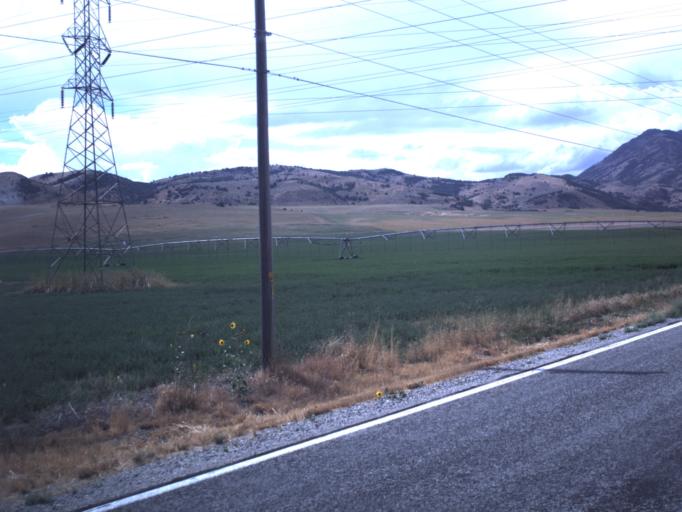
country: US
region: Utah
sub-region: Cache County
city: Benson
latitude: 41.8792
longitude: -112.0249
